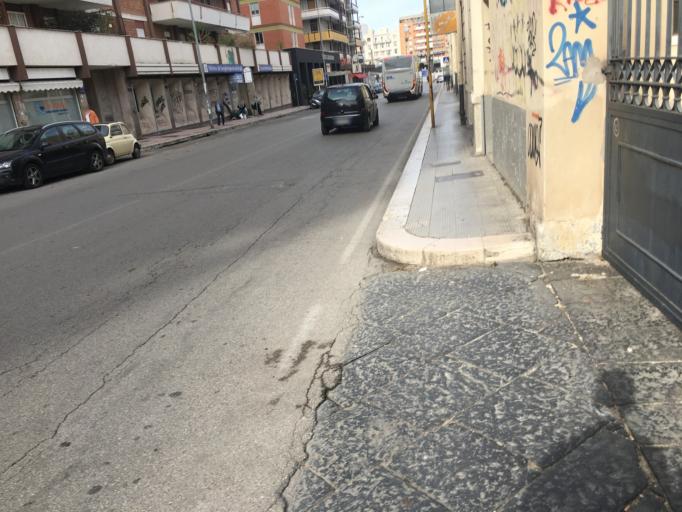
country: IT
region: Apulia
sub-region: Provincia di Bari
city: Bari
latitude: 41.1158
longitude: 16.8688
